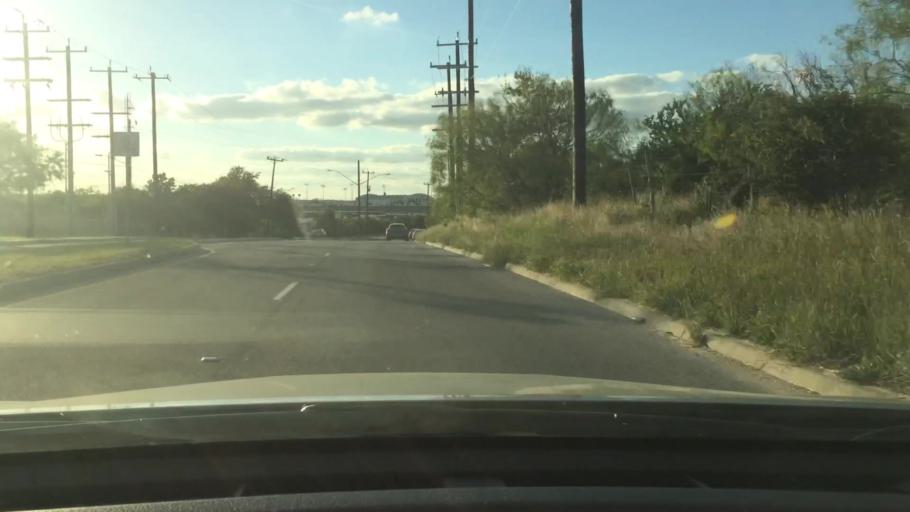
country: US
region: Texas
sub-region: Bexar County
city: Hollywood Park
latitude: 29.5469
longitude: -98.4587
